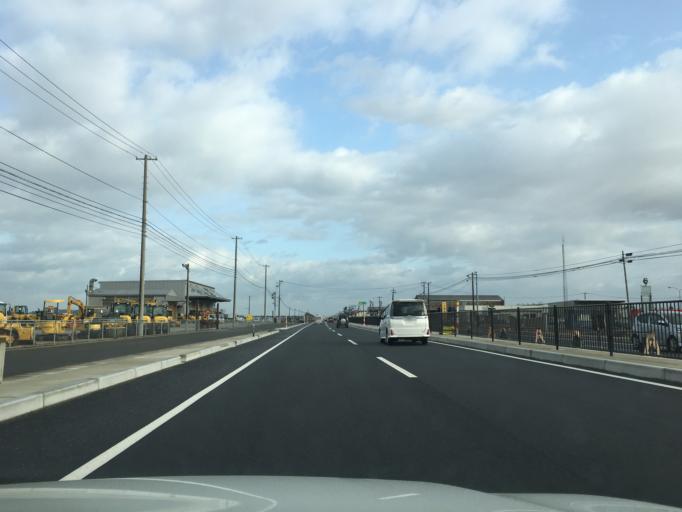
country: JP
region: Yamagata
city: Sakata
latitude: 38.8519
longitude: 139.8475
